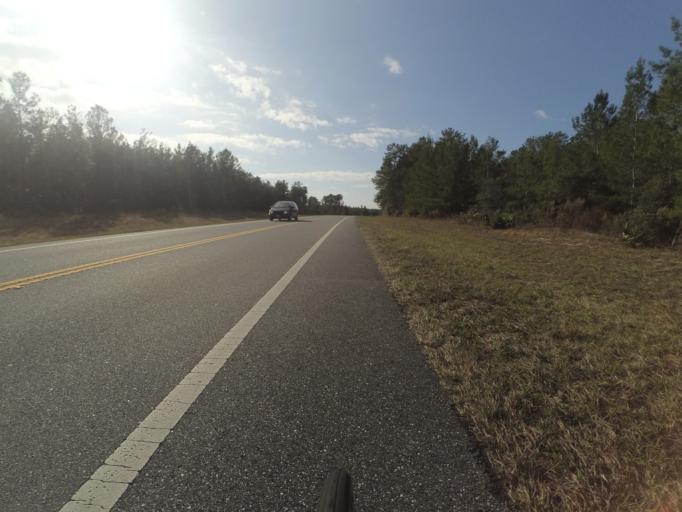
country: US
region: Florida
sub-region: Lake County
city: Astor
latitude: 29.1105
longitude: -81.6172
